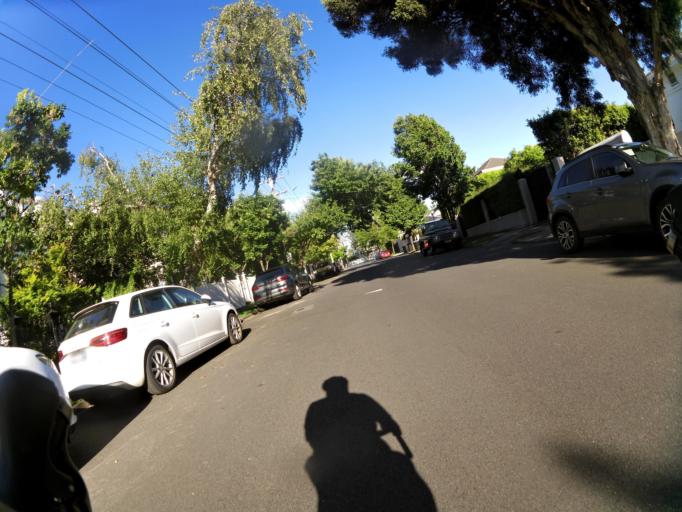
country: AU
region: Victoria
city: Toorak
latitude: -37.8513
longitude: 145.0199
